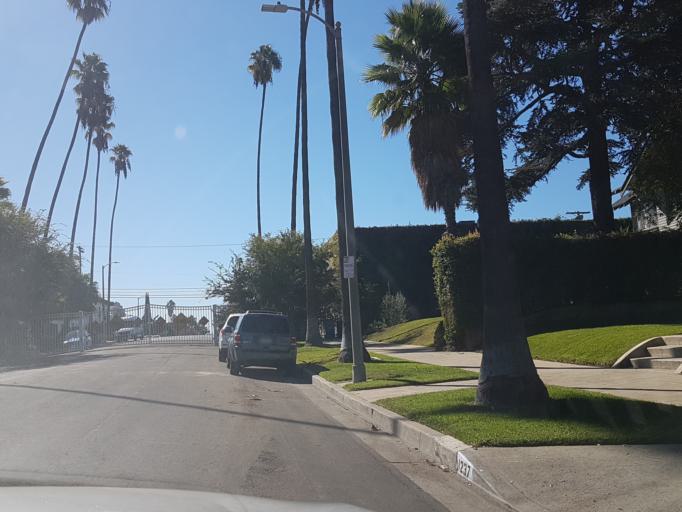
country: US
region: California
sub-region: Los Angeles County
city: Hollywood
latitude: 34.0481
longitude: -118.3158
